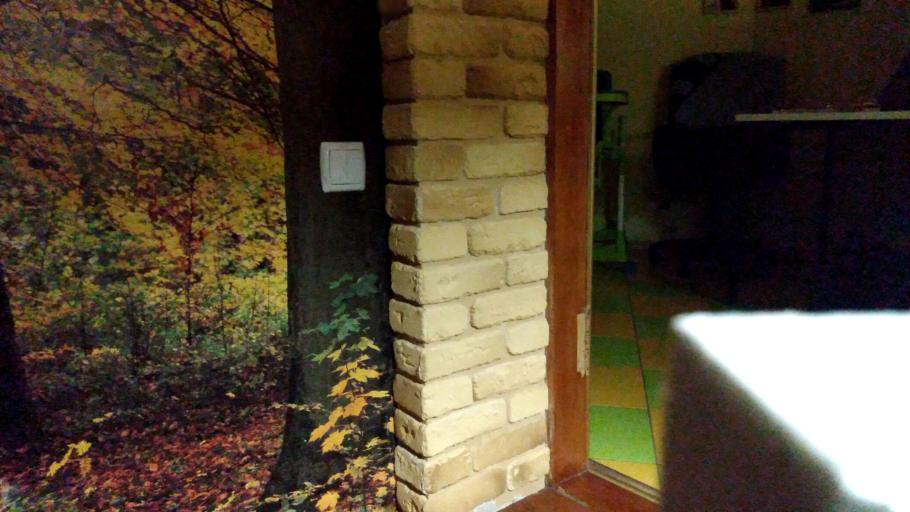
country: RU
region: Vologda
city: Lipin Bor
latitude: 60.7524
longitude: 38.0503
